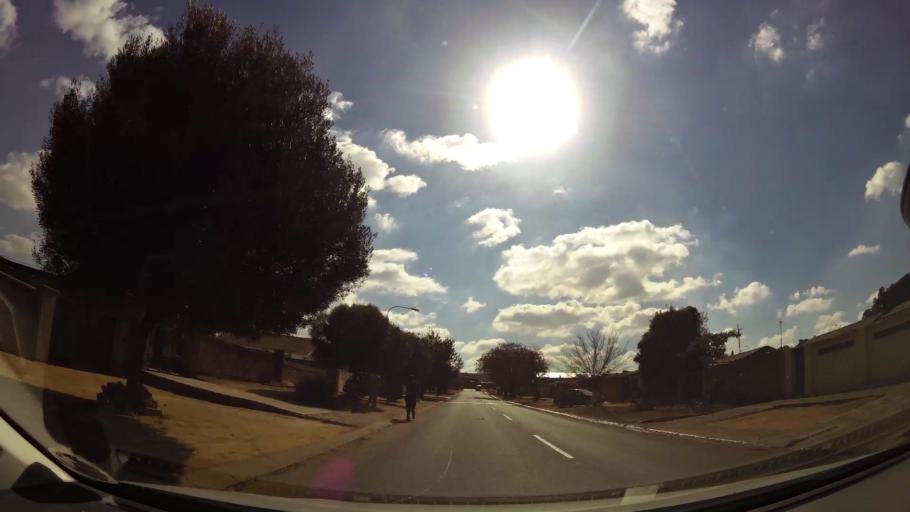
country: ZA
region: Gauteng
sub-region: City of Johannesburg Metropolitan Municipality
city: Roodepoort
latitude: -26.2081
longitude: 27.8805
